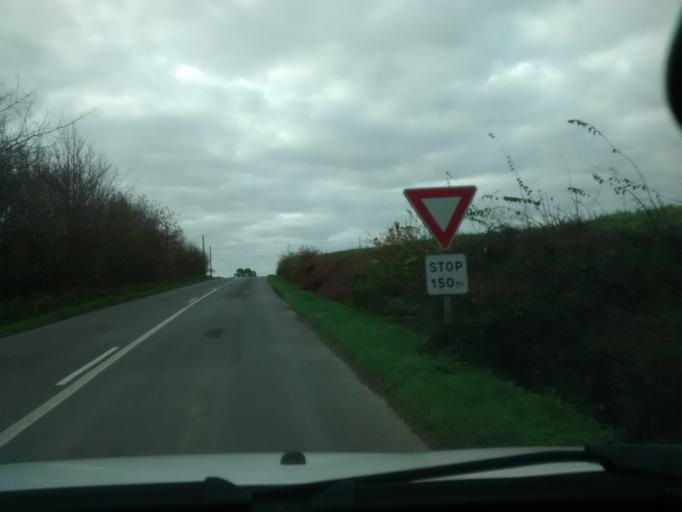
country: FR
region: Brittany
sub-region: Departement d'Ille-et-Vilaine
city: Chavagne
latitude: 48.0674
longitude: -1.7686
